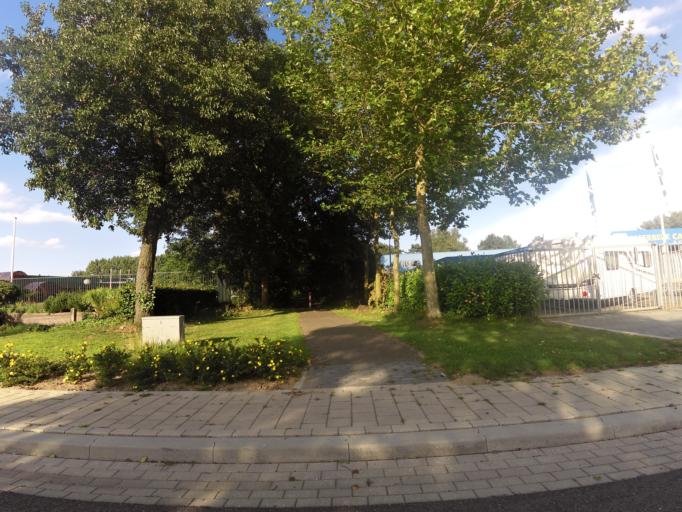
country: NL
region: Gelderland
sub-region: Gemeente Doetinchem
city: Doetinchem
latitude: 51.9488
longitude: 6.2962
